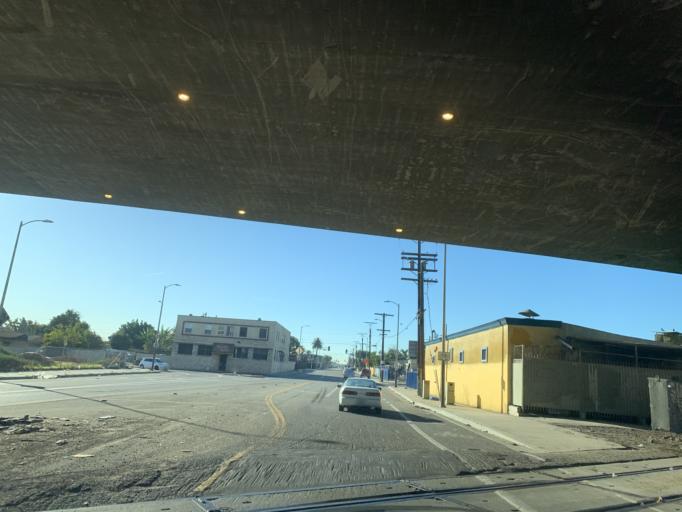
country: US
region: California
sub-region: Los Angeles County
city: West Athens
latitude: 33.9281
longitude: -118.2783
